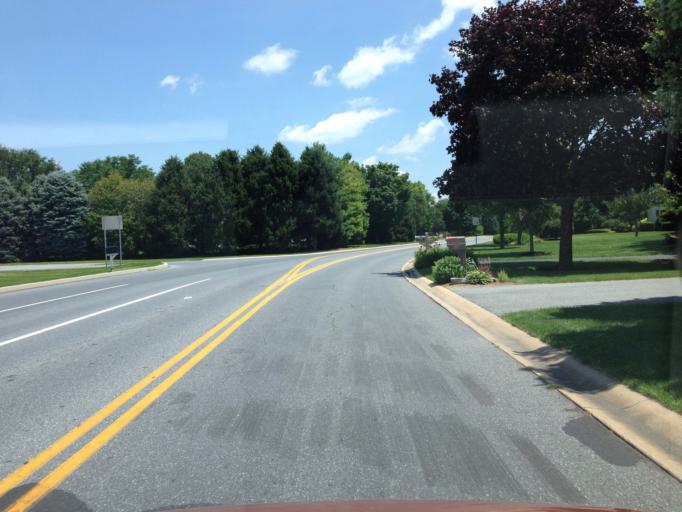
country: US
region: Pennsylvania
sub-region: Lancaster County
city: East Petersburg
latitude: 40.1091
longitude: -76.3344
